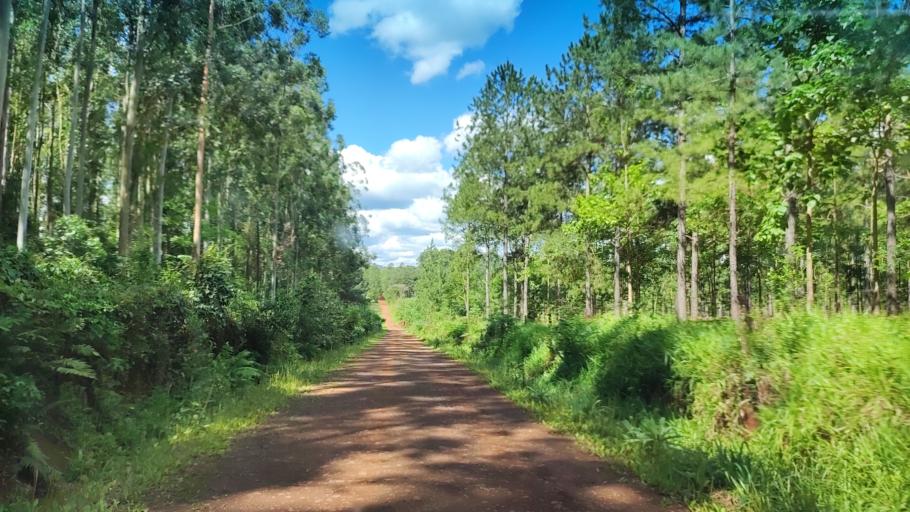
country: AR
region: Misiones
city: Ruiz de Montoya
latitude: -26.9528
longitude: -55.0129
